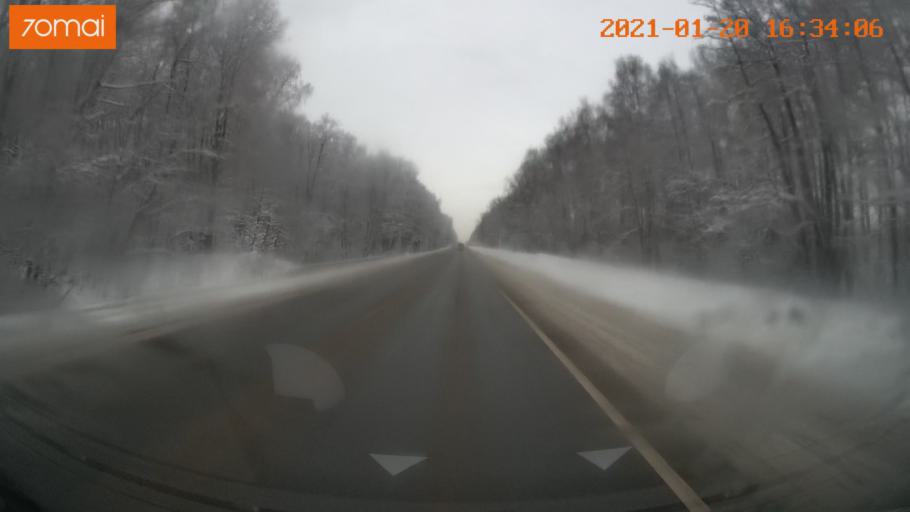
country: RU
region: Vladimir
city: Orgtrud
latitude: 56.2017
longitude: 40.7842
